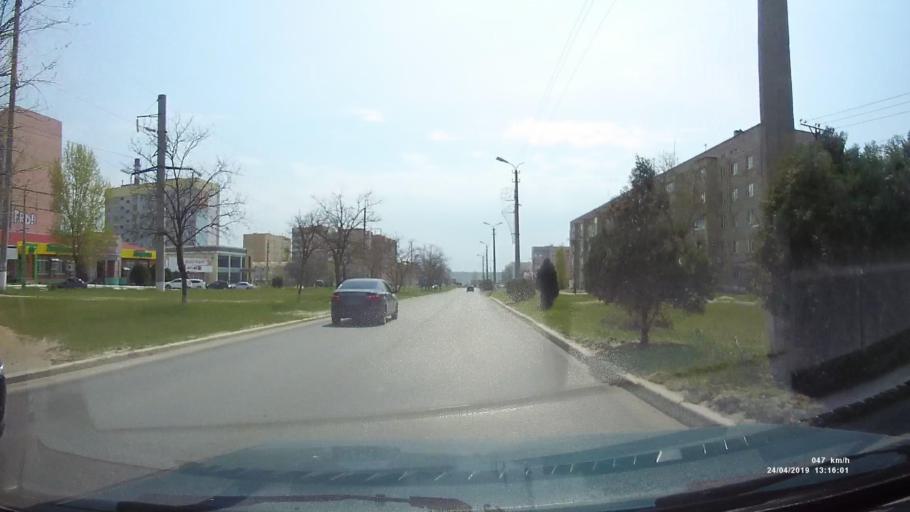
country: RU
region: Kalmykiya
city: Elista
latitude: 46.3060
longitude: 44.3046
